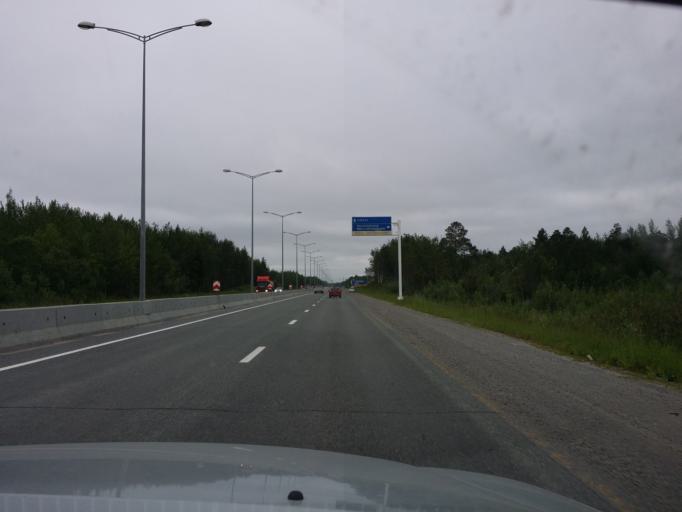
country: RU
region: Khanty-Mansiyskiy Avtonomnyy Okrug
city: Nizhnevartovsk
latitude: 61.0031
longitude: 76.4151
